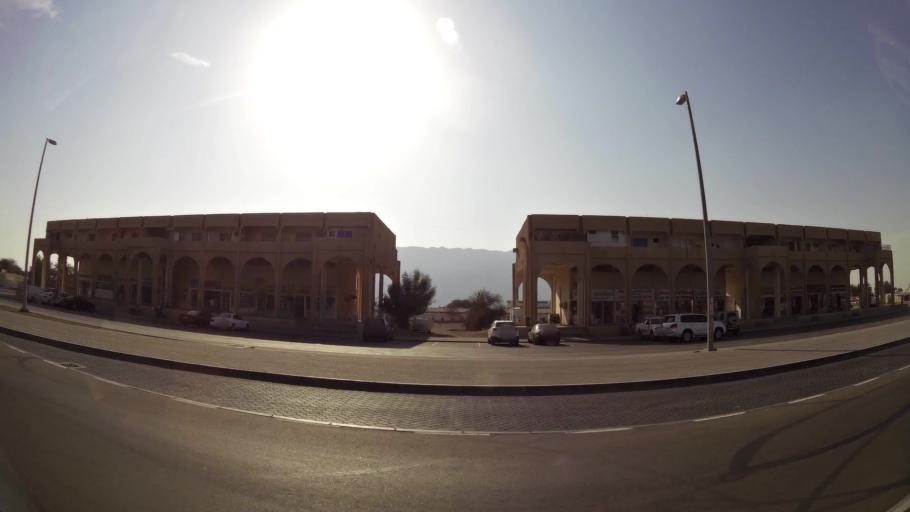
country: AE
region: Abu Dhabi
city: Al Ain
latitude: 24.0395
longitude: 55.8436
